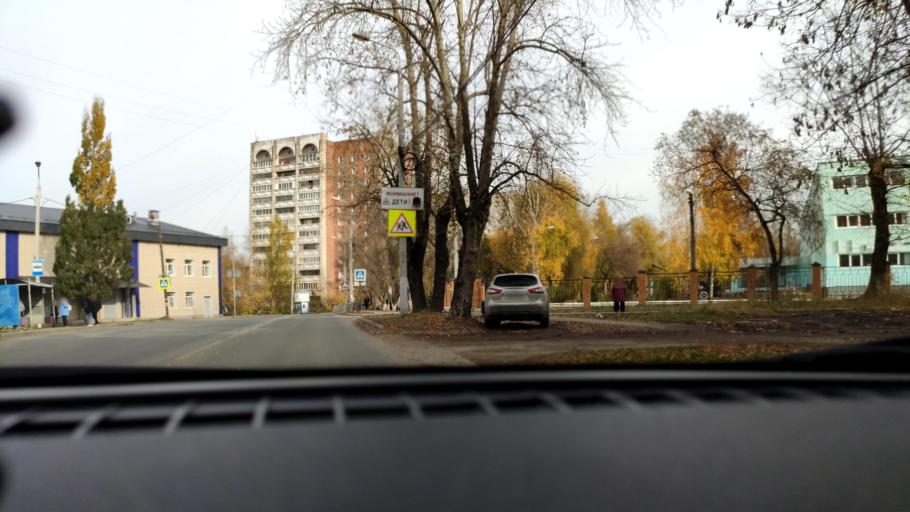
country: RU
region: Perm
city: Perm
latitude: 58.0661
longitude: 56.3557
